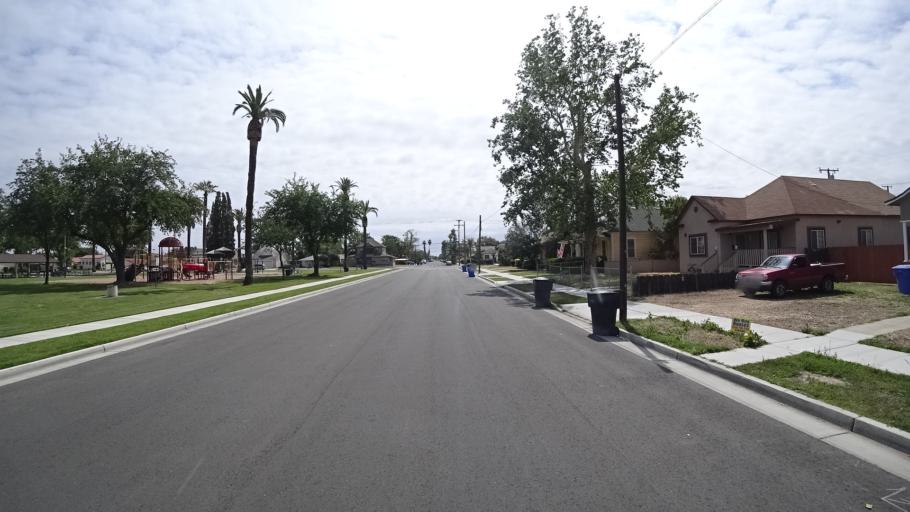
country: US
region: California
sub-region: Kings County
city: Hanford
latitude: 36.3340
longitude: -119.6454
